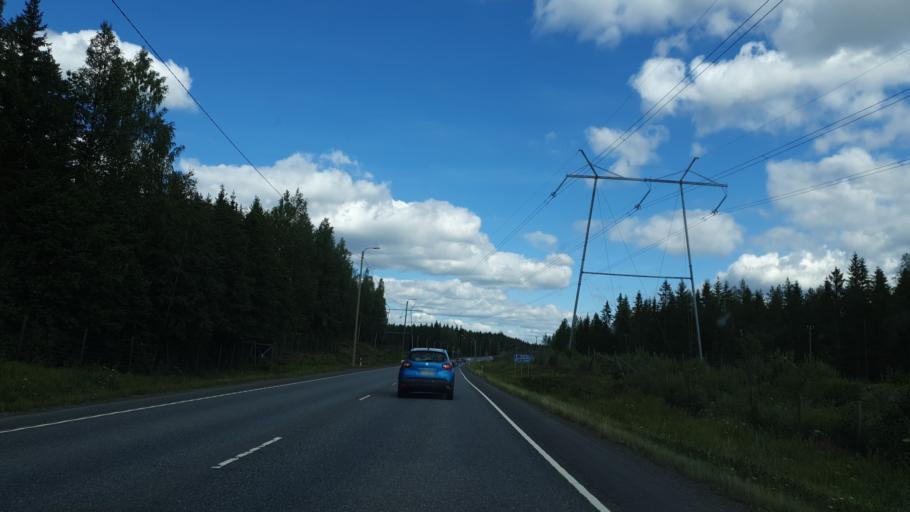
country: FI
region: Pirkanmaa
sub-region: Tampere
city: Orivesi
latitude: 61.6320
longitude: 24.1835
